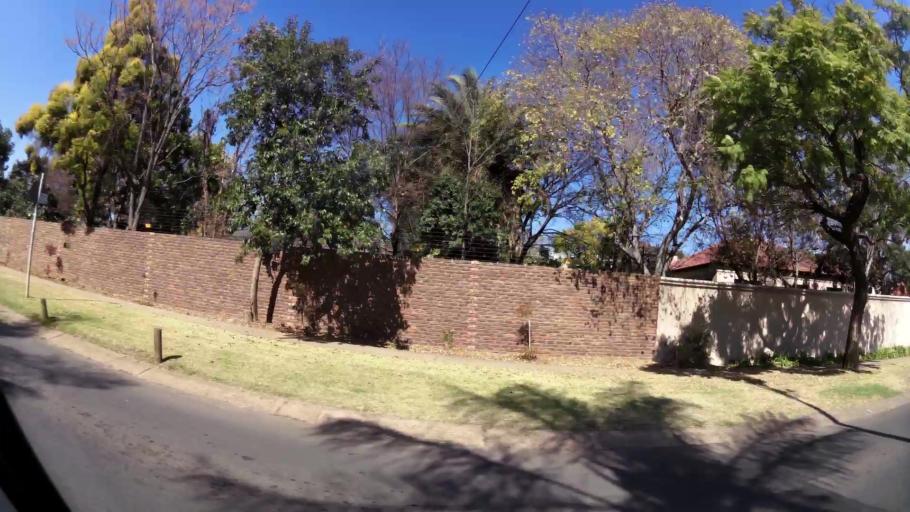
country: ZA
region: Gauteng
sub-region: City of Tshwane Metropolitan Municipality
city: Pretoria
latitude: -25.7787
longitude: 28.2477
